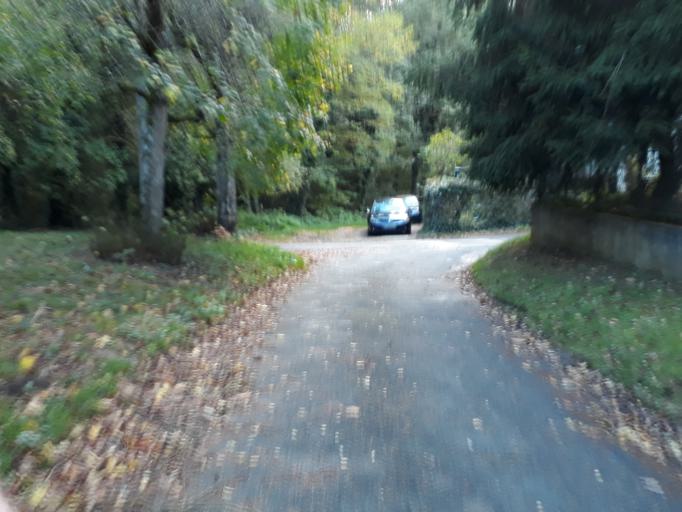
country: FR
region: Ile-de-France
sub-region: Departement de Seine-et-Marne
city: Bois-le-Roi
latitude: 48.4638
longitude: 2.6984
